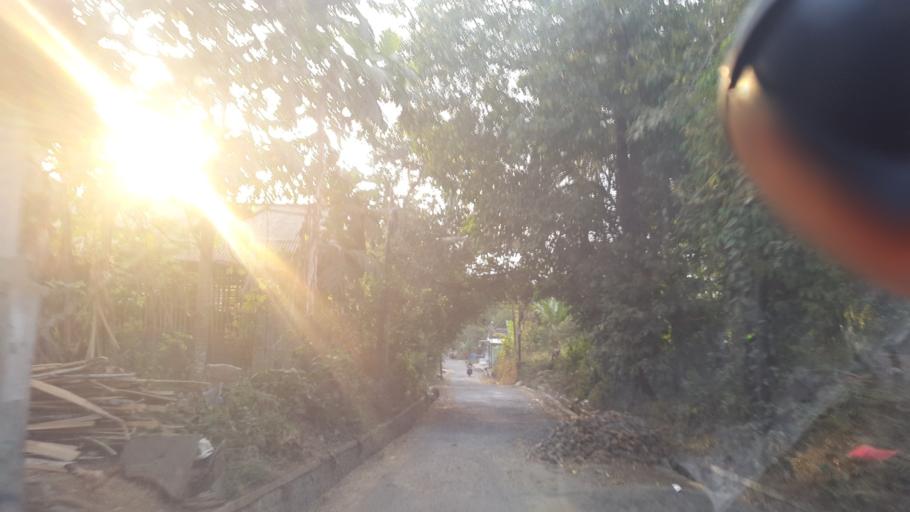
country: ID
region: West Java
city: Karajeun
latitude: -7.2155
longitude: 106.8649
